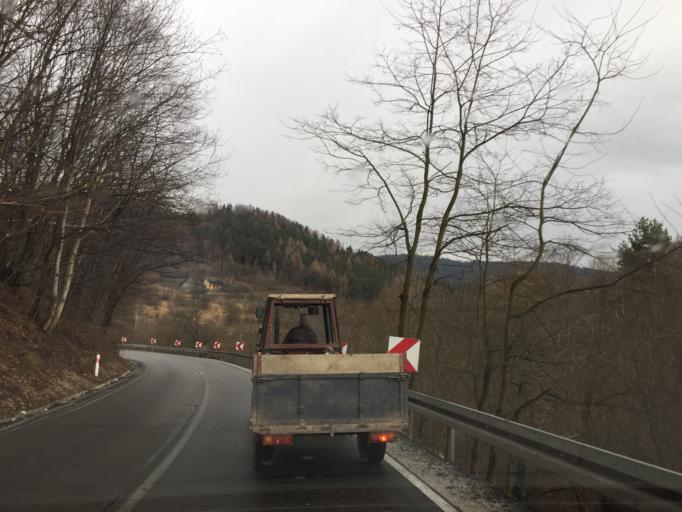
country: PL
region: Lesser Poland Voivodeship
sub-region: Powiat myslenicki
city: Harbutowice
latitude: 49.8049
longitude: 19.7666
